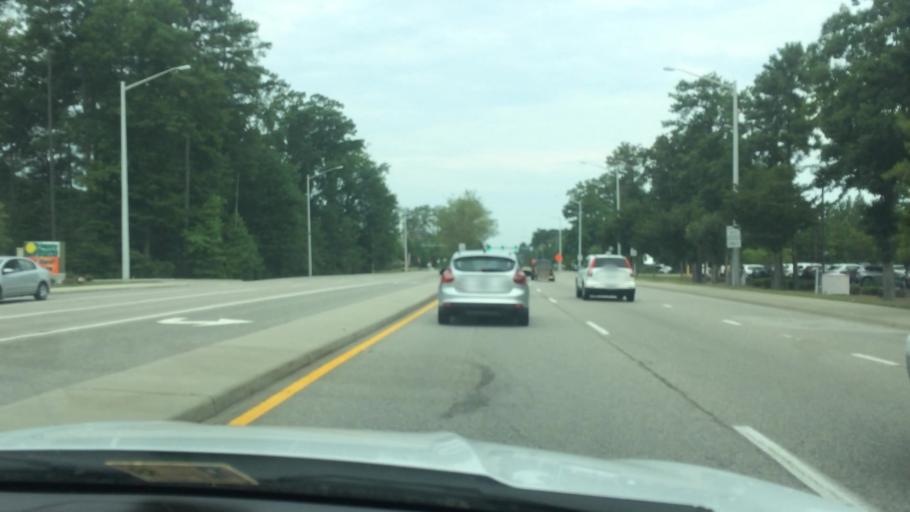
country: US
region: Virginia
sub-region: York County
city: Yorktown
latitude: 37.1557
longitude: -76.5334
